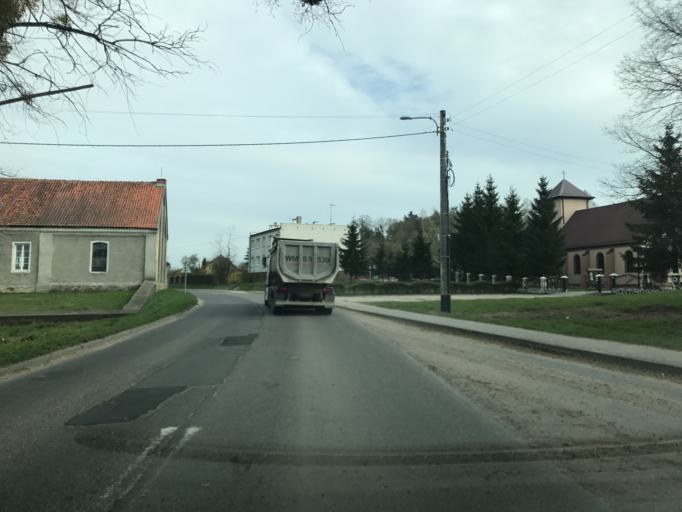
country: PL
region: Warmian-Masurian Voivodeship
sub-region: Powiat ostrodzki
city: Gierzwald
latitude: 53.5420
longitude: 20.0889
